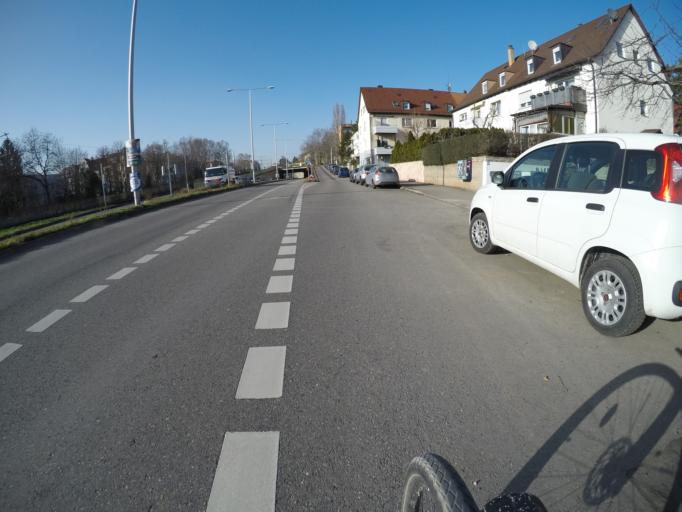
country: DE
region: Baden-Wuerttemberg
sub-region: Regierungsbezirk Stuttgart
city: Stuttgart-Ost
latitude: 48.8043
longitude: 9.2320
